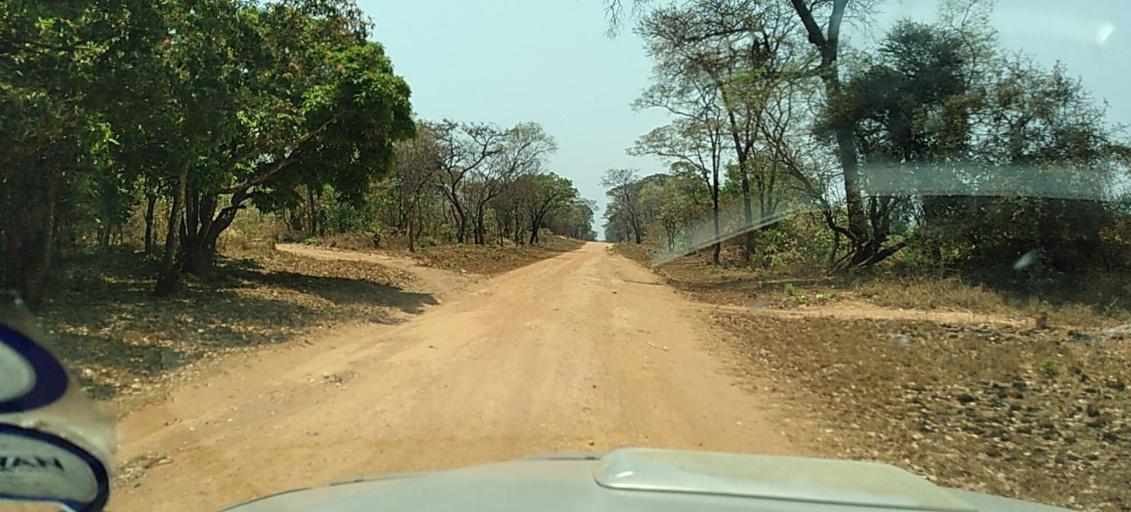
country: ZM
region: North-Western
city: Kasempa
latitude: -13.5489
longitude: 26.0313
